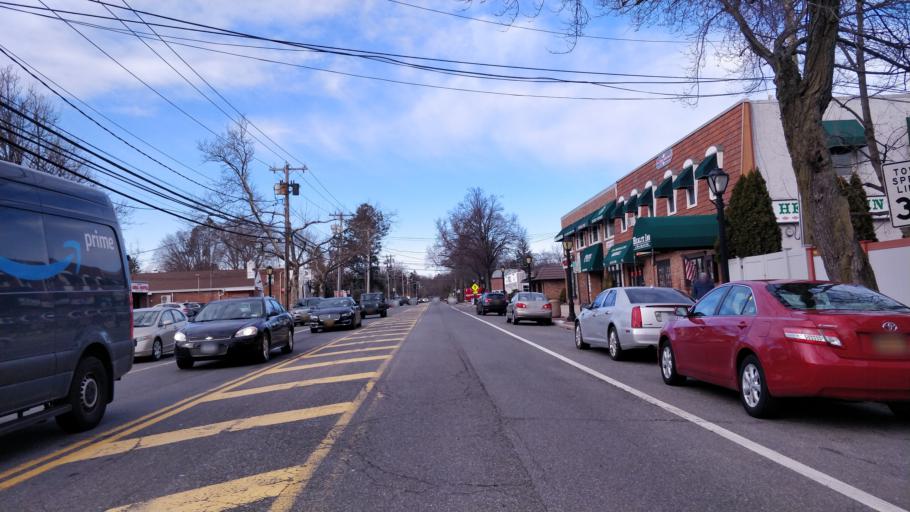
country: US
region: New York
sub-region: Suffolk County
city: Greenlawn
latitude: 40.8692
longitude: -73.3651
